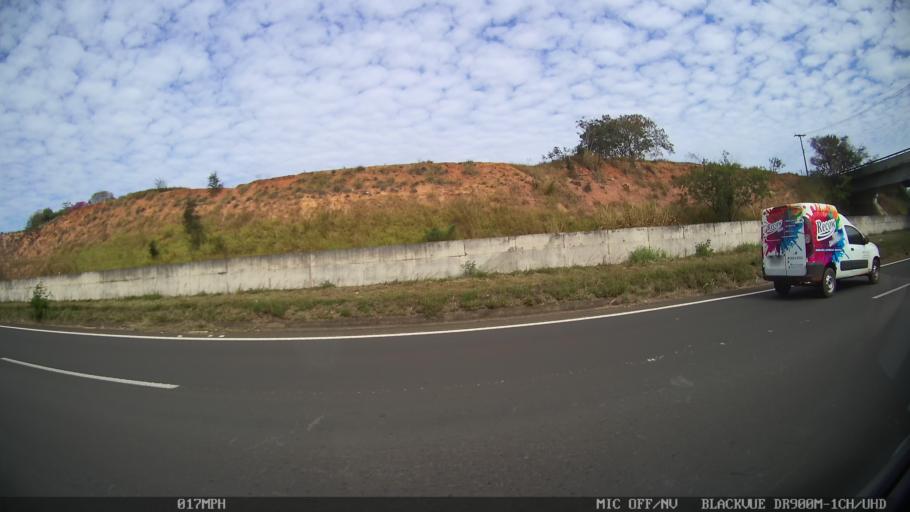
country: BR
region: Sao Paulo
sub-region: Santa Barbara D'Oeste
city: Santa Barbara d'Oeste
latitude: -22.7664
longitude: -47.4194
